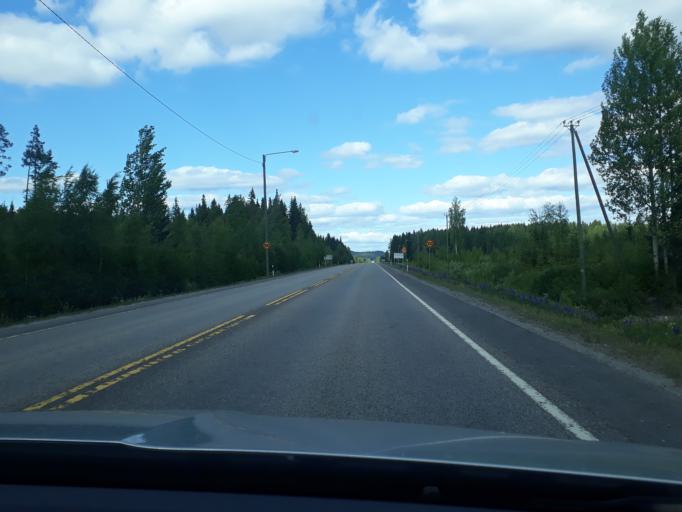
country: FI
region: Central Finland
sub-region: AEaenekoski
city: AEaenekoski
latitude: 62.6467
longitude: 25.7103
